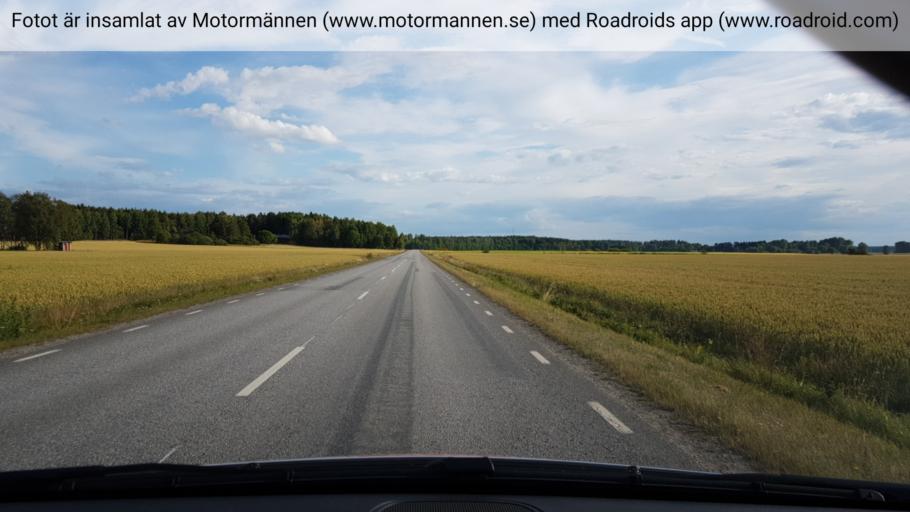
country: SE
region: Vaestmanland
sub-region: Vasteras
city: Skultuna
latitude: 59.7517
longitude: 16.4551
